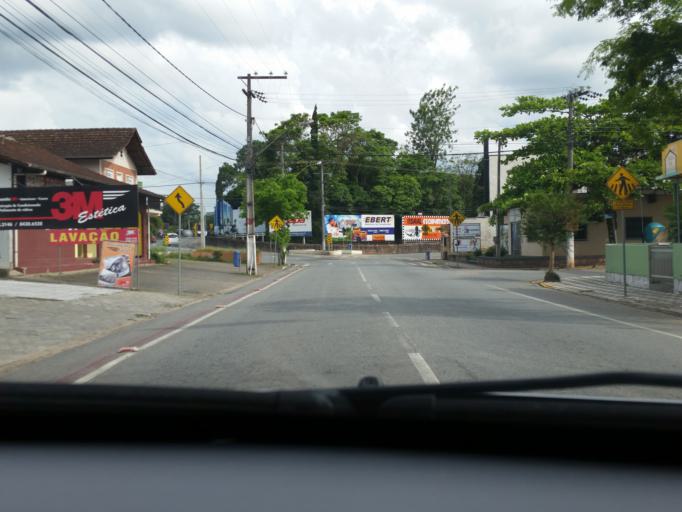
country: BR
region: Santa Catarina
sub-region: Indaial
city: Indaial
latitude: -26.8920
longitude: -49.2426
